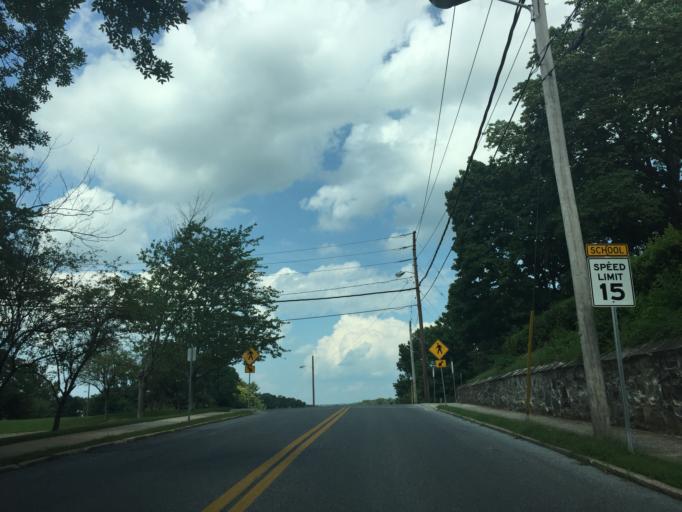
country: US
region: Maryland
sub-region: Carroll County
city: Westminster
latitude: 39.5751
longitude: -76.9914
